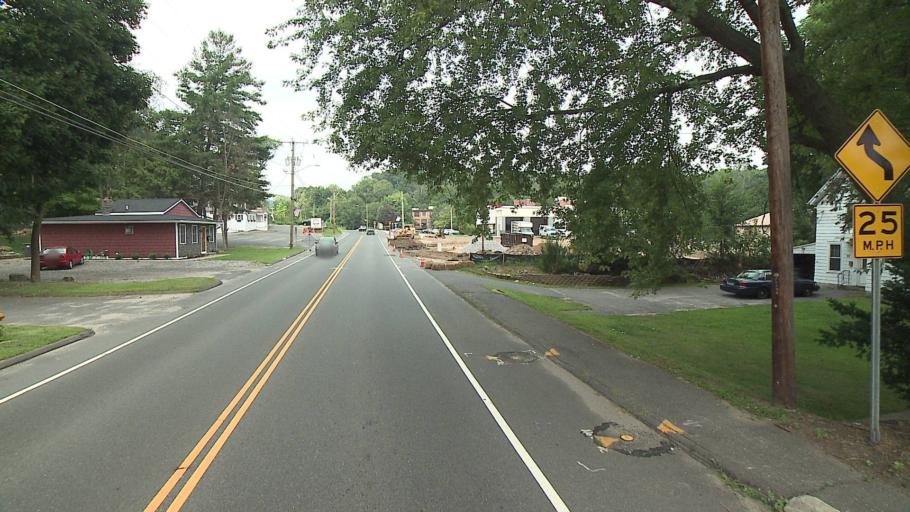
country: US
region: Connecticut
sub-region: Litchfield County
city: Oakville
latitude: 41.5901
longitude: -73.0951
